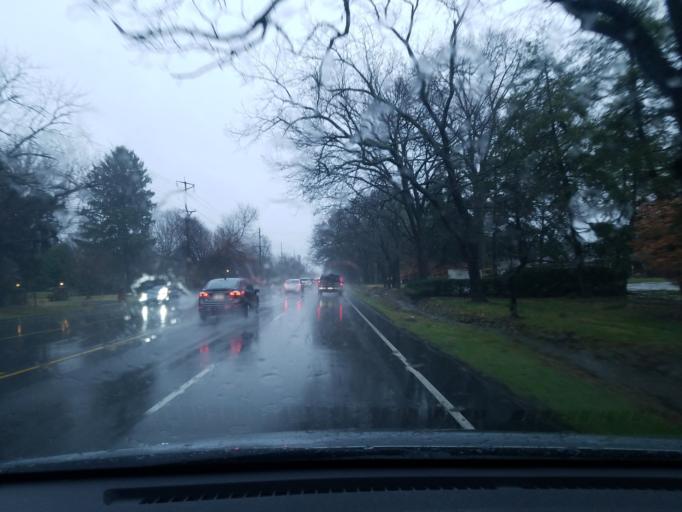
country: US
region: Kentucky
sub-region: Jefferson County
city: Hurstbourne
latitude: 38.2476
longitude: -85.5928
